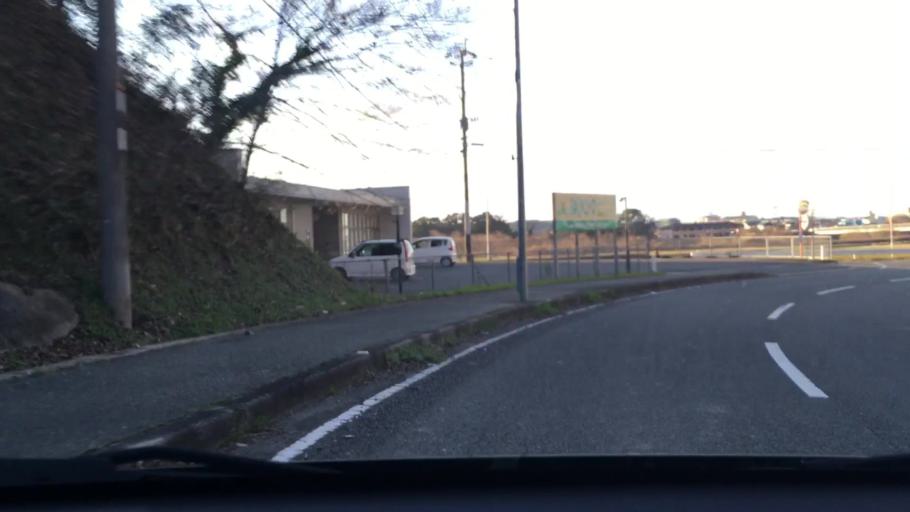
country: JP
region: Oita
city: Bungo-Takada-shi
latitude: 33.5180
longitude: 131.3487
